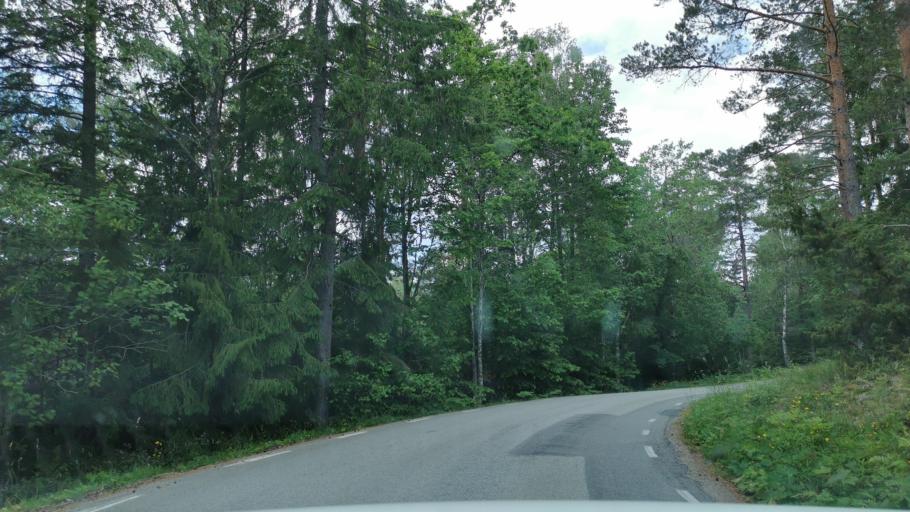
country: SE
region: Vaestra Goetaland
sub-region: Bengtsfors Kommun
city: Dals Langed
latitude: 58.8684
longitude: 12.4022
